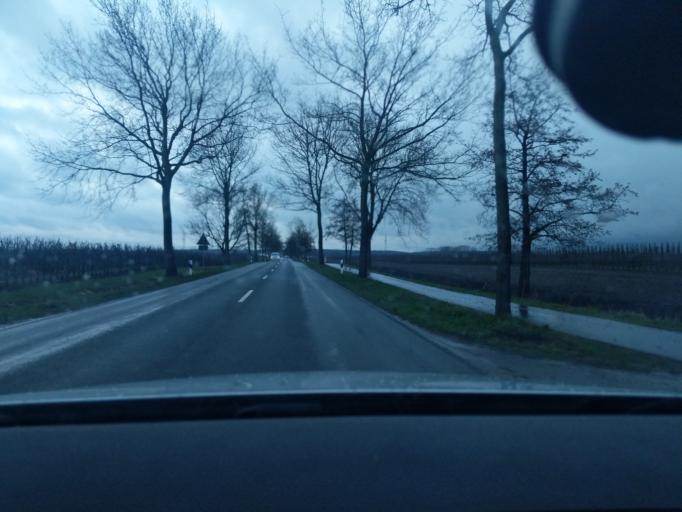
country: DE
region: Lower Saxony
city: Jork
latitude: 53.5096
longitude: 9.6654
